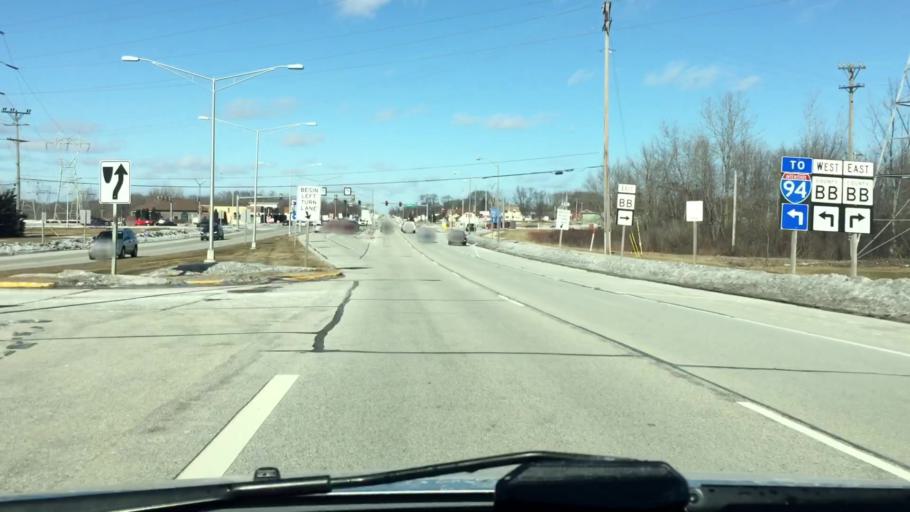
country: US
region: Wisconsin
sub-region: Milwaukee County
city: South Milwaukee
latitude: 42.9138
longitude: -87.9109
